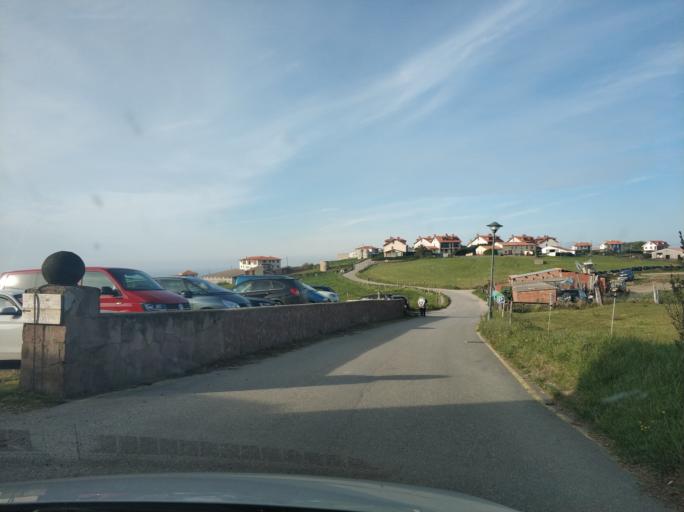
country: ES
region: Cantabria
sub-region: Provincia de Cantabria
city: San Vicente de la Barquera
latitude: 43.3963
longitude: -4.3510
